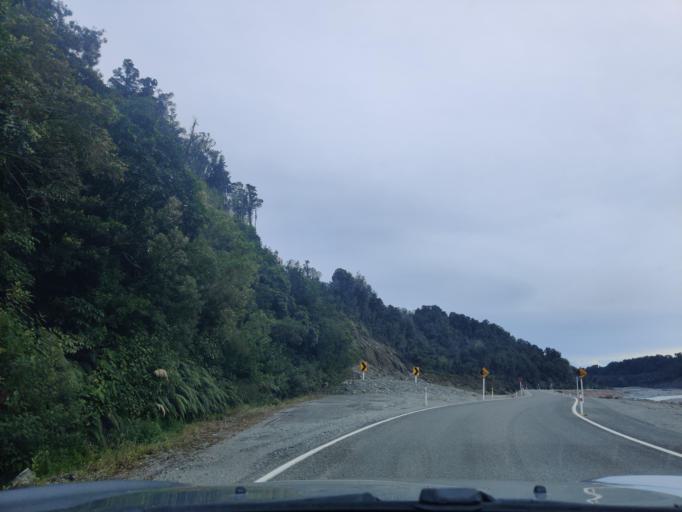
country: NZ
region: West Coast
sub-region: Westland District
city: Hokitika
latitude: -43.4065
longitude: 170.1775
